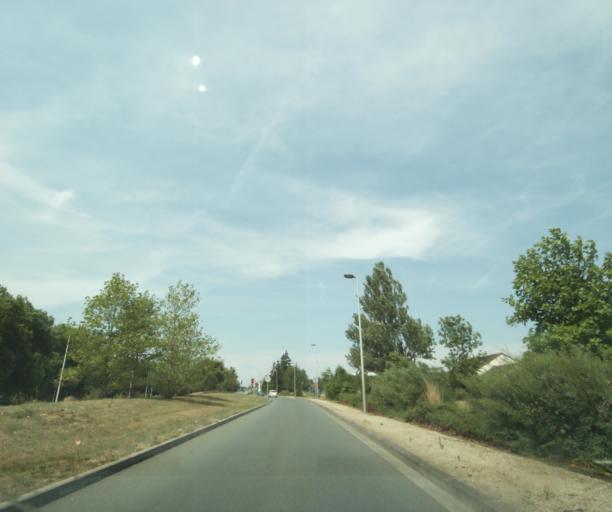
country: FR
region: Poitou-Charentes
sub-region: Departement de la Vienne
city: Antran
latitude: 46.8800
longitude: 0.5672
